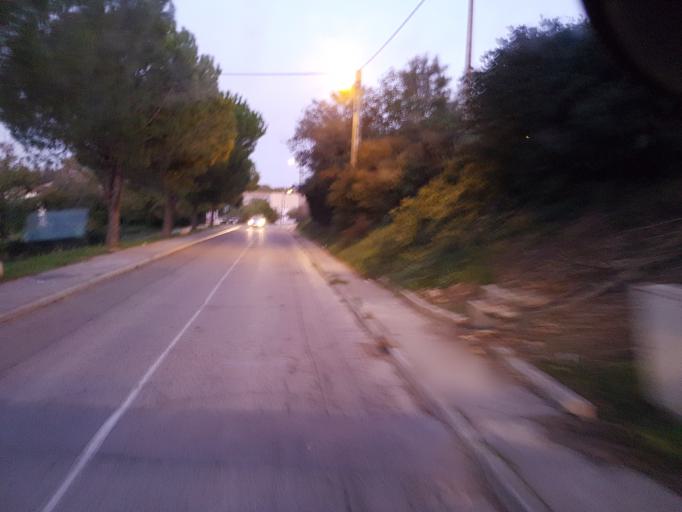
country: FR
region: Languedoc-Roussillon
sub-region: Departement du Gard
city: Bellegarde
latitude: 43.7570
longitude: 4.5087
